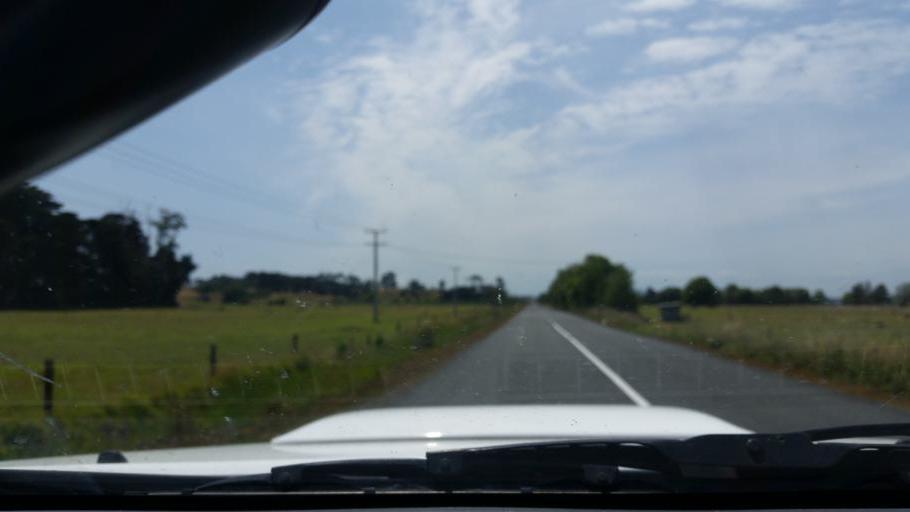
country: NZ
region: Northland
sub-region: Kaipara District
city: Dargaville
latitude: -36.0671
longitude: 173.9403
